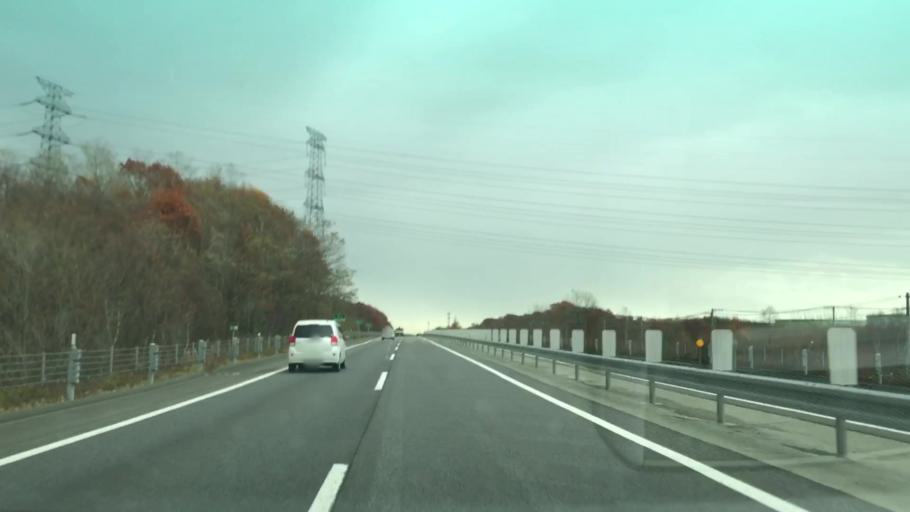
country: JP
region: Hokkaido
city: Tomakomai
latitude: 42.6641
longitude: 141.8080
